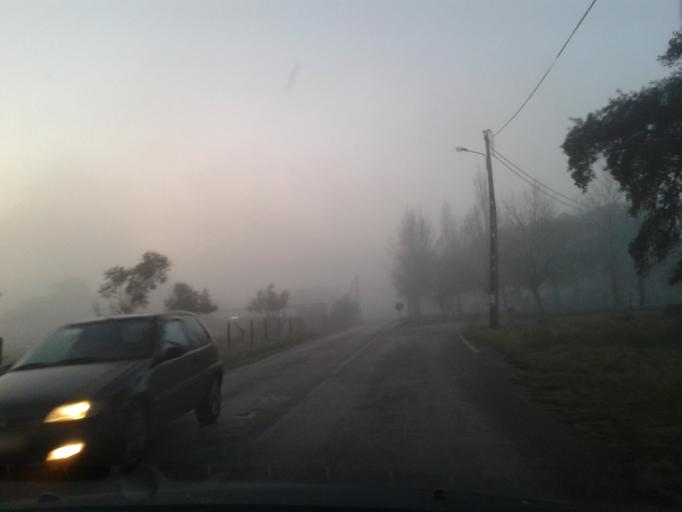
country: PT
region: Setubal
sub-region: Palmela
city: Palmela
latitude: 38.5991
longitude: -8.8965
